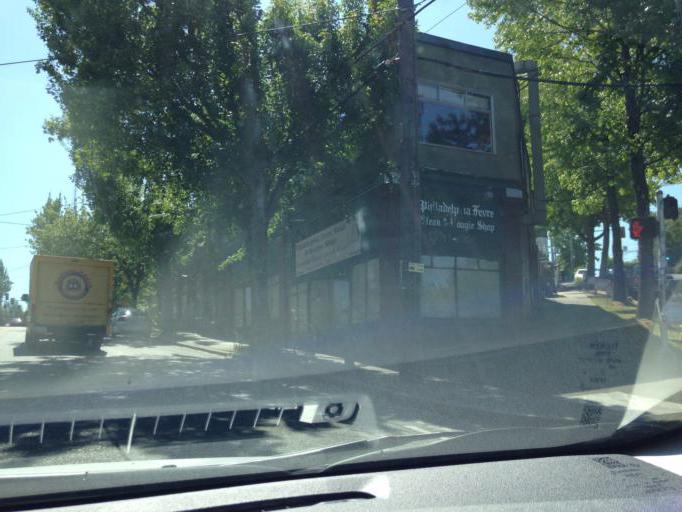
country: US
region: Washington
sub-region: King County
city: Seattle
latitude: 47.6202
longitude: -122.3012
